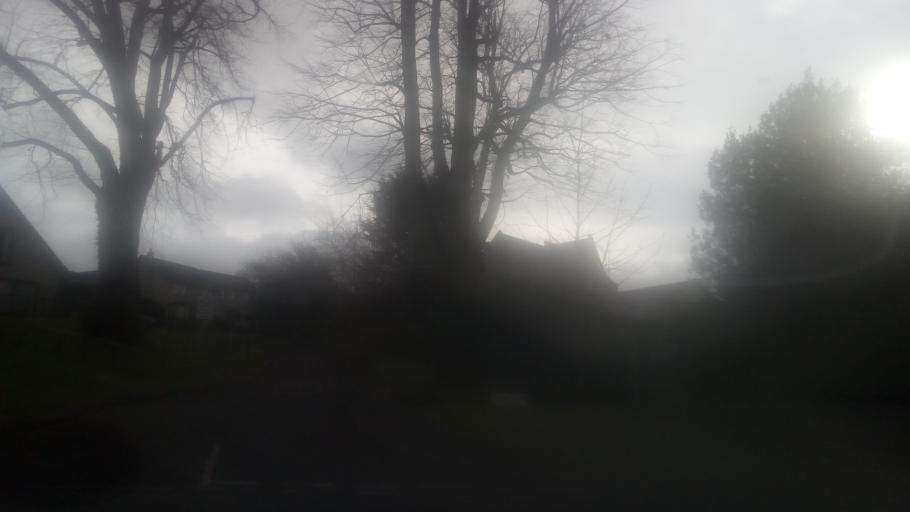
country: GB
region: Scotland
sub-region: The Scottish Borders
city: Jedburgh
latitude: 55.4760
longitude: -2.5505
